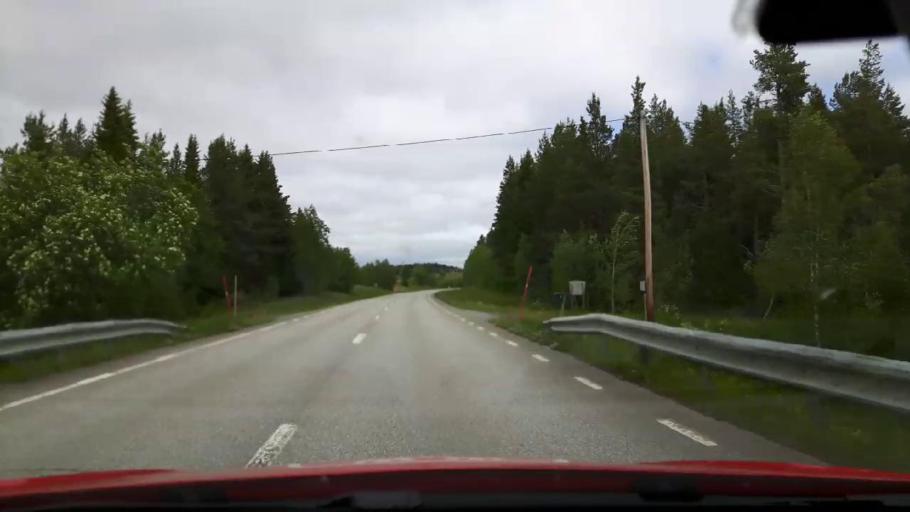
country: SE
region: Jaemtland
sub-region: Krokoms Kommun
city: Krokom
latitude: 63.5103
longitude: 14.5196
